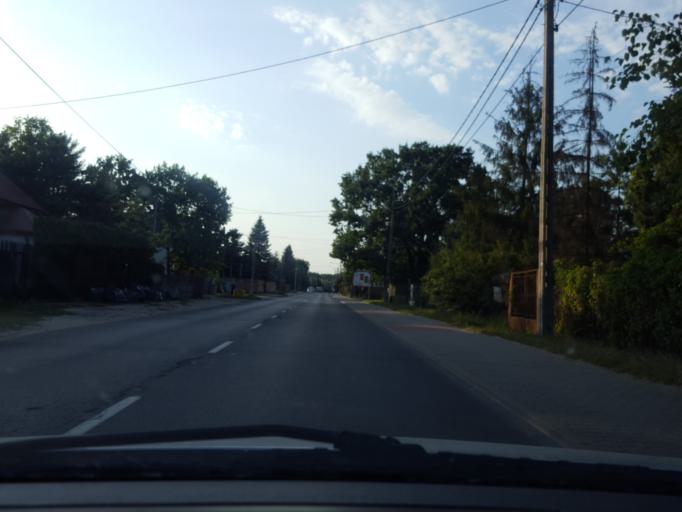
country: PL
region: Masovian Voivodeship
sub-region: Warszawa
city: Rembertow
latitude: 52.2683
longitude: 21.1527
